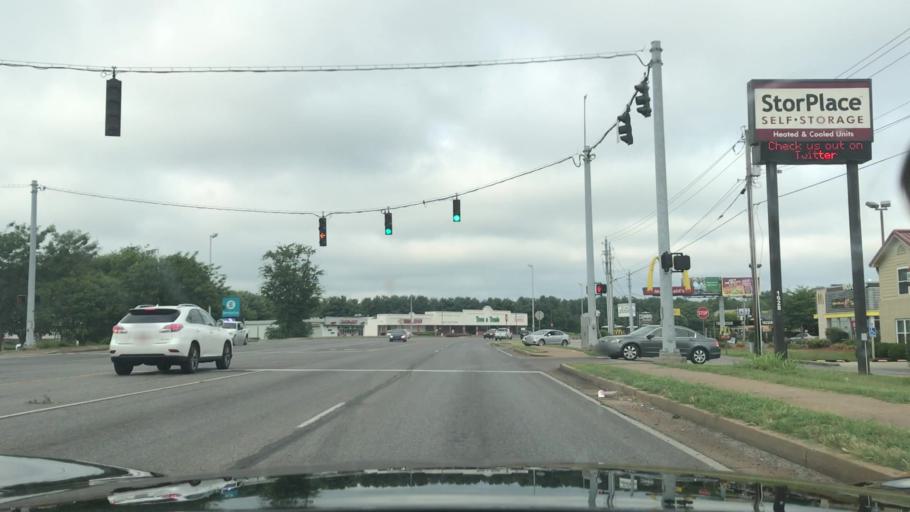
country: US
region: Kentucky
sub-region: Warren County
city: Bowling Green
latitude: 36.9513
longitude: -86.4376
